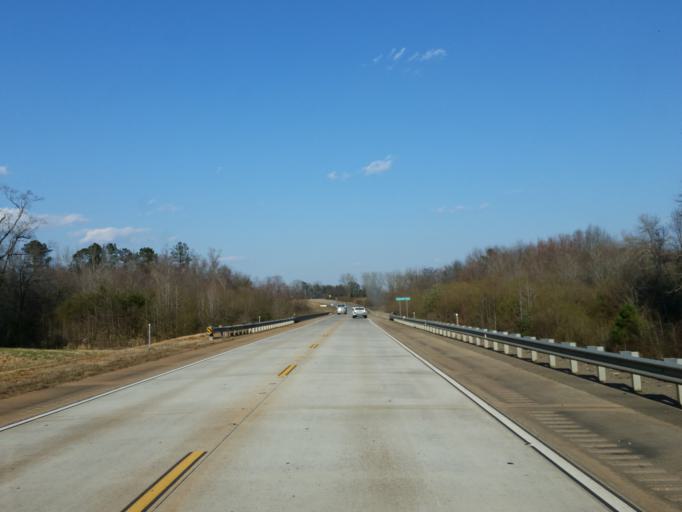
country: US
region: Georgia
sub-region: Lamar County
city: Barnesville
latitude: 33.0365
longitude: -84.1382
